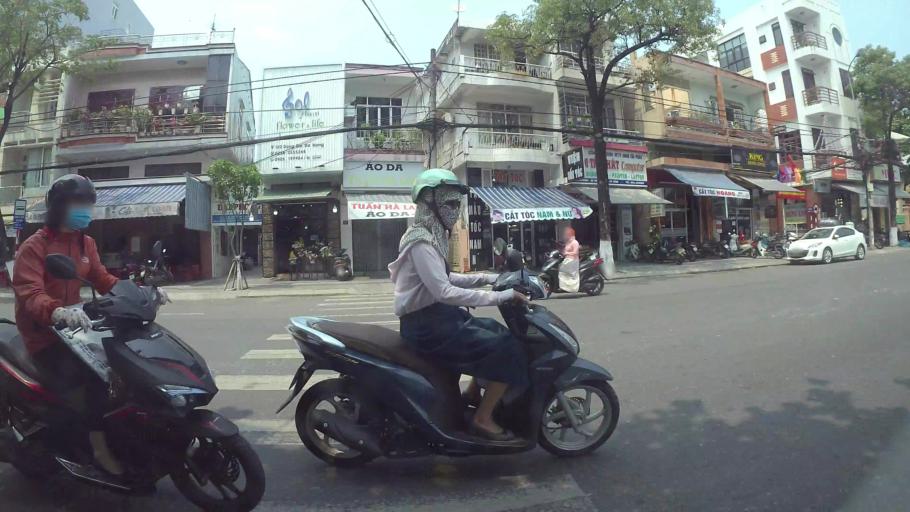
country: VN
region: Da Nang
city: Da Nang
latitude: 16.0809
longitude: 108.2189
